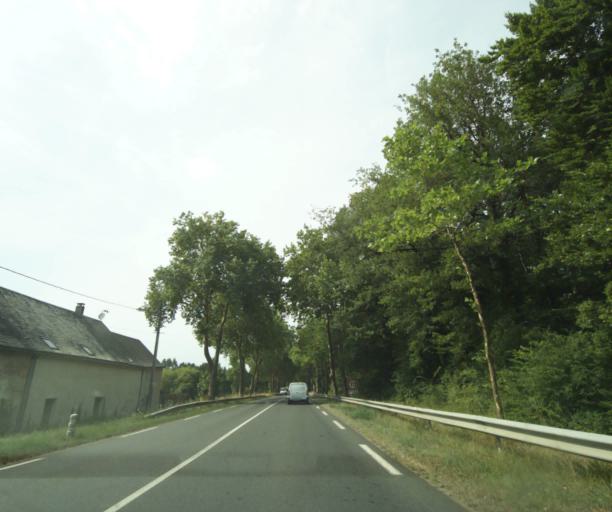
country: FR
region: Centre
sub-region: Departement d'Indre-et-Loire
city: Charentilly
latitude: 47.4706
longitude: 0.6174
